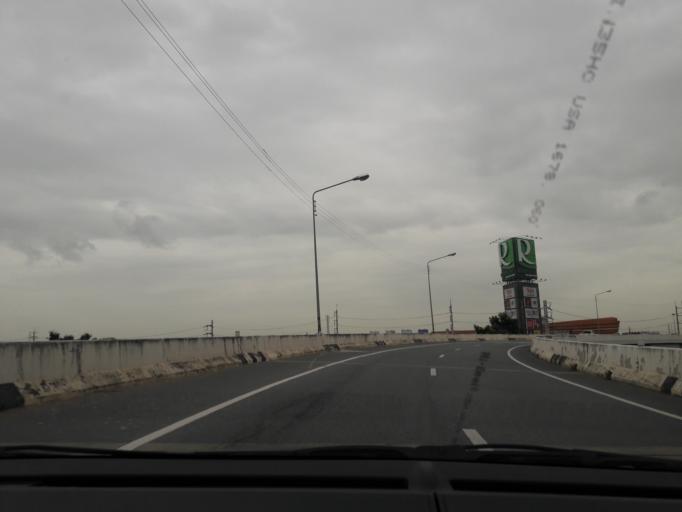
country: TH
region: Sara Buri
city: Saraburi
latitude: 14.5394
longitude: 100.9537
